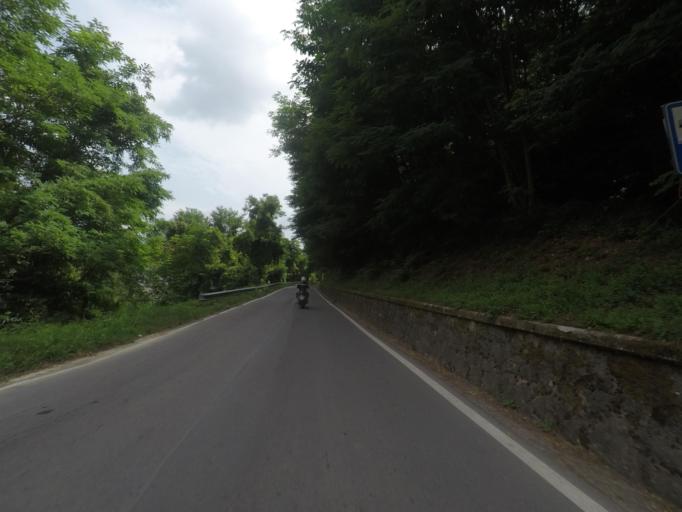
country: IT
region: Tuscany
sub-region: Provincia di Lucca
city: Castelnuovo di Garfagnana
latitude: 44.1093
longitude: 10.3982
